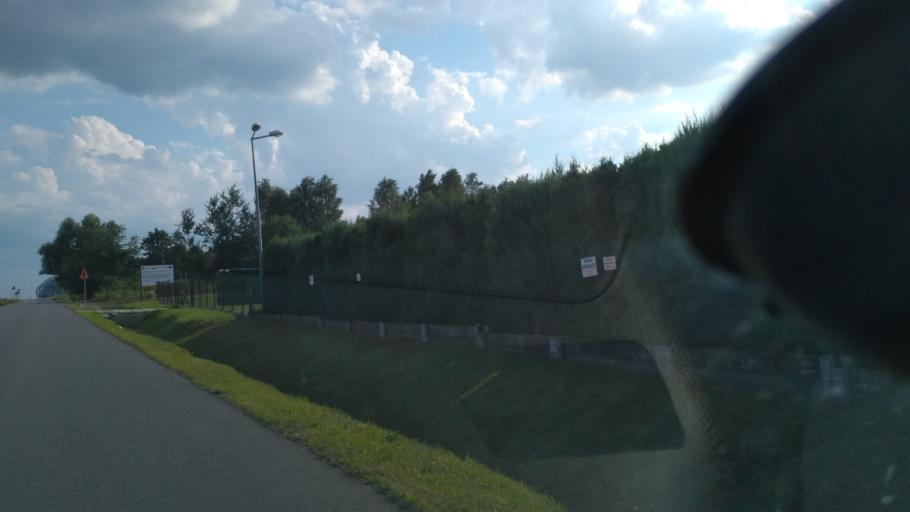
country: PL
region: Subcarpathian Voivodeship
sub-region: Powiat rzeszowski
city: Wysoka Glogowska
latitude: 50.1239
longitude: 22.0245
